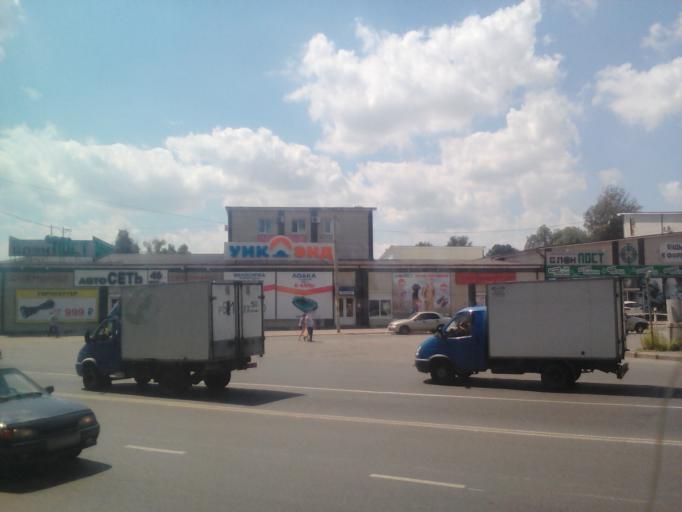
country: RU
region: Kursk
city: Kursk
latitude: 51.7195
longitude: 36.1884
